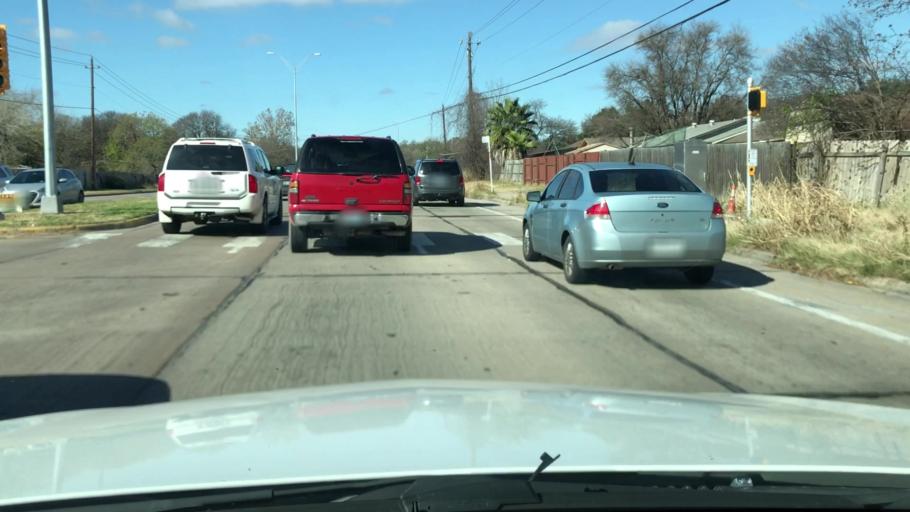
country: US
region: Texas
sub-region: Travis County
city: Onion Creek
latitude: 30.1810
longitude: -97.7502
